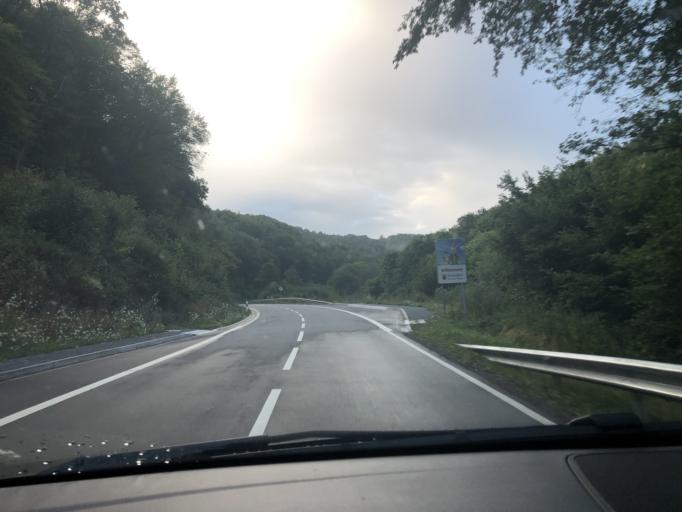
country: DE
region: Rheinland-Pfalz
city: Grimburg
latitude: 49.6036
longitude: 6.8772
